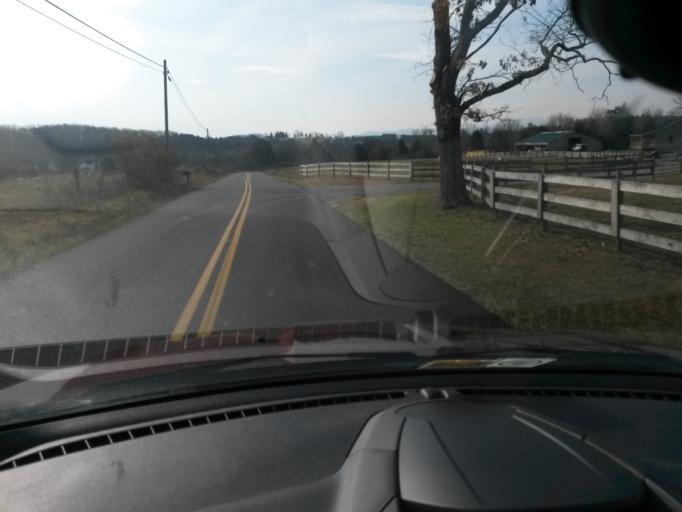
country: US
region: Virginia
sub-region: Botetourt County
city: Fincastle
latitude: 37.5413
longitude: -79.8748
